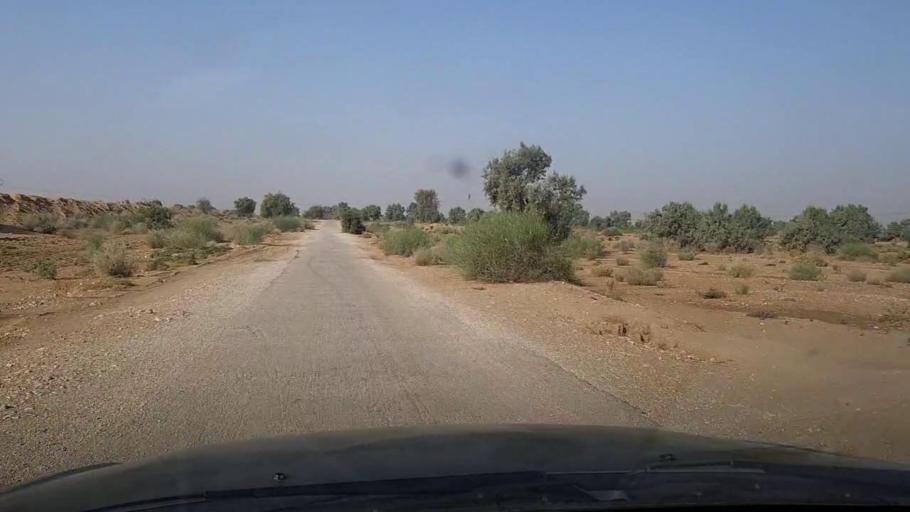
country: PK
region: Sindh
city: Sann
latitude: 26.0210
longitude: 68.1033
